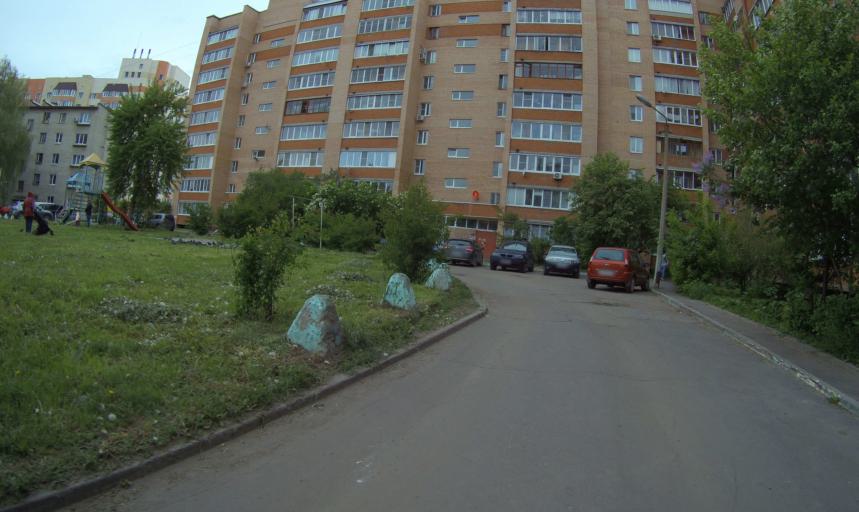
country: RU
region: Moskovskaya
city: Kolomna
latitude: 55.0805
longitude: 38.8061
